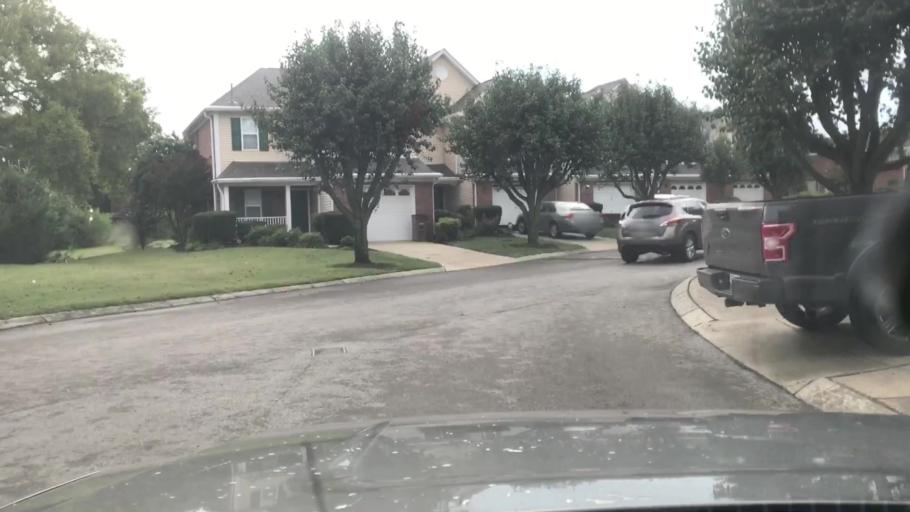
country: US
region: Tennessee
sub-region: Rutherford County
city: La Vergne
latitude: 36.0904
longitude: -86.6315
